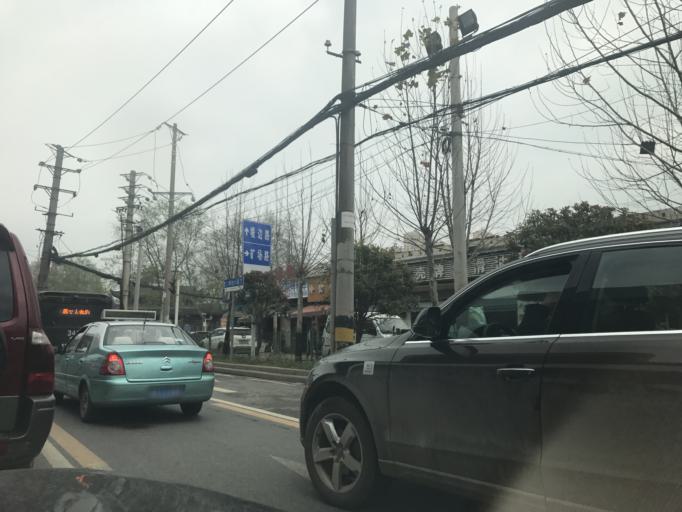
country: CN
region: Hubei
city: Houhu
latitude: 30.6603
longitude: 114.3299
